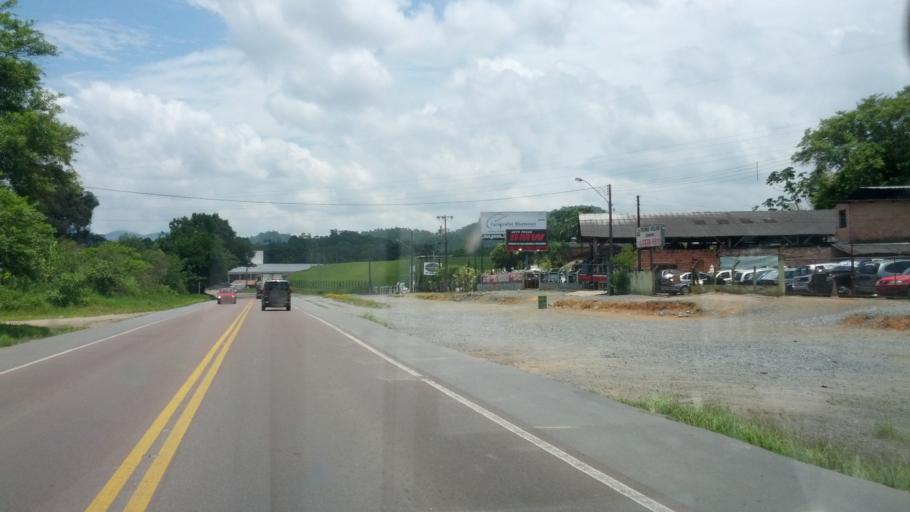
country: BR
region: Santa Catarina
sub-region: Blumenau
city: Blumenau
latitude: -26.8673
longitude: -49.1025
